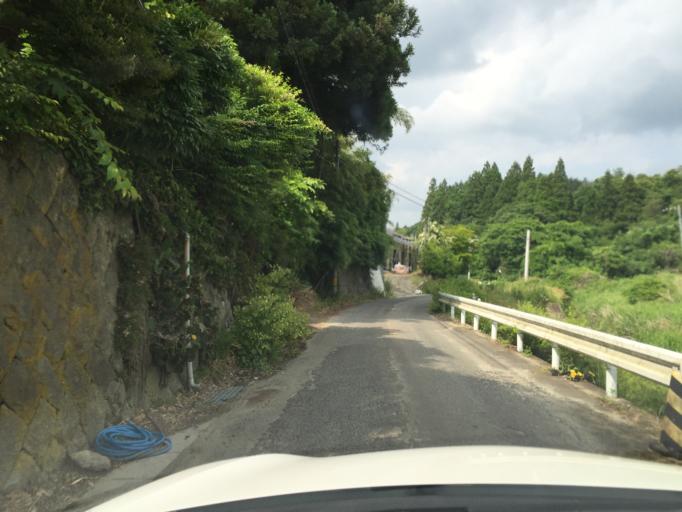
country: JP
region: Fukushima
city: Sukagawa
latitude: 37.3196
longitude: 140.4589
